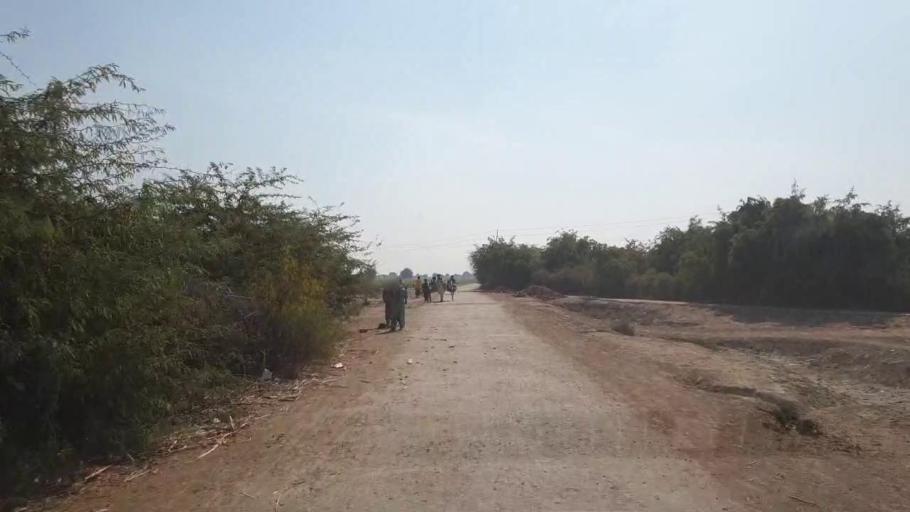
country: PK
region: Sindh
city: Chambar
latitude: 25.3386
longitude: 68.8116
